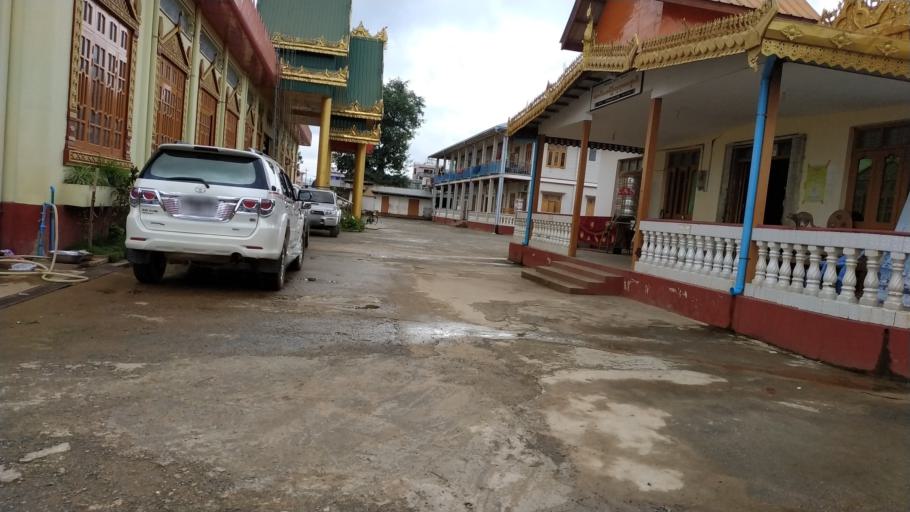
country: MM
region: Shan
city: Lashio
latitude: 22.4922
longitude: 98.3953
